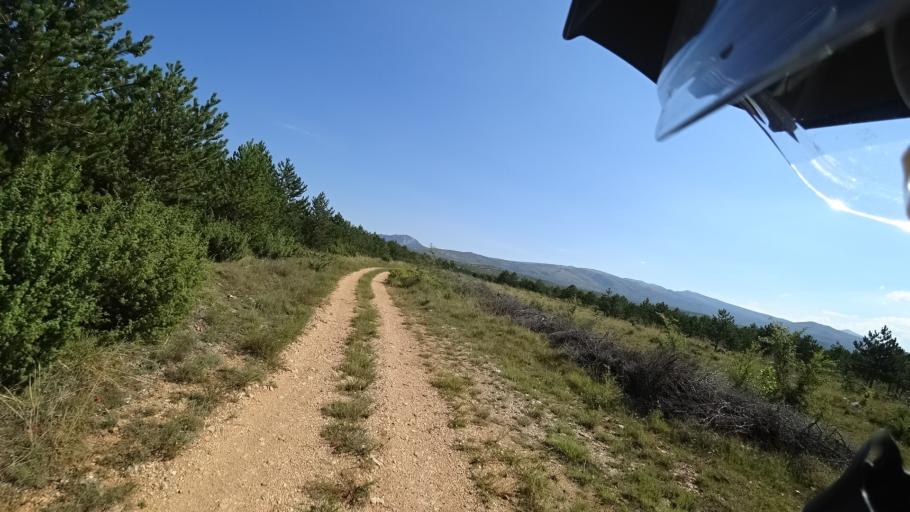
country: HR
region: Sibensko-Kniniska
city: Drnis
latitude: 43.8627
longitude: 16.2526
